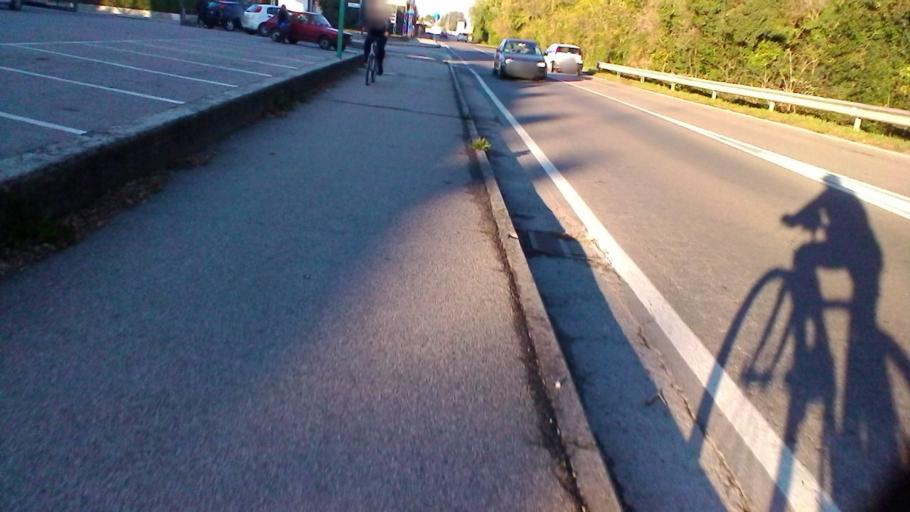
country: IT
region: Veneto
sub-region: Provincia di Verona
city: Povegliano Veronese
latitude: 45.3507
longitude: 10.8887
